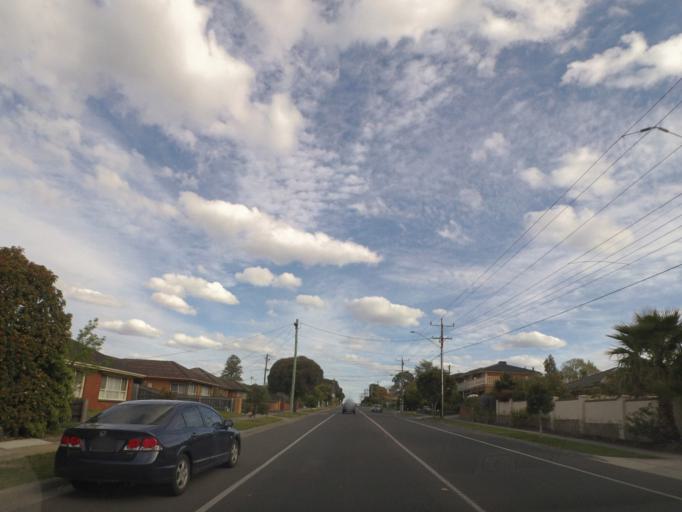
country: AU
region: Victoria
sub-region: Manningham
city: Doncaster East
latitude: -37.7837
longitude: 145.1443
